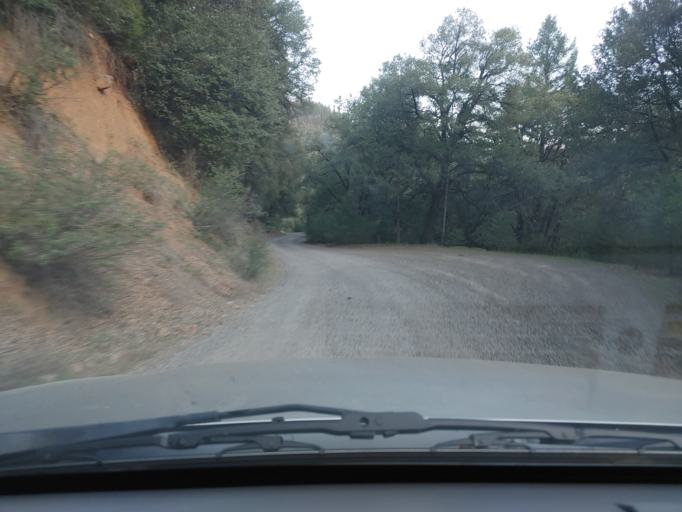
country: US
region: California
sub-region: Shasta County
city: Bella Vista
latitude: 40.8388
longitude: -122.0241
